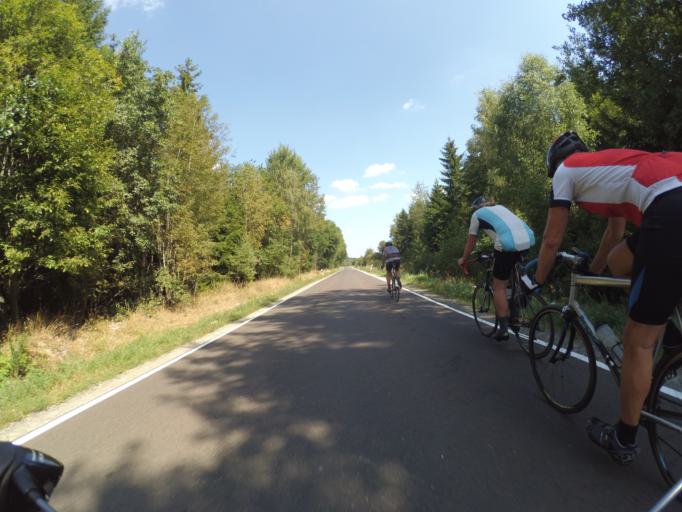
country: DE
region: Rheinland-Pfalz
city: Schauren
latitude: 49.8191
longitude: 7.2551
